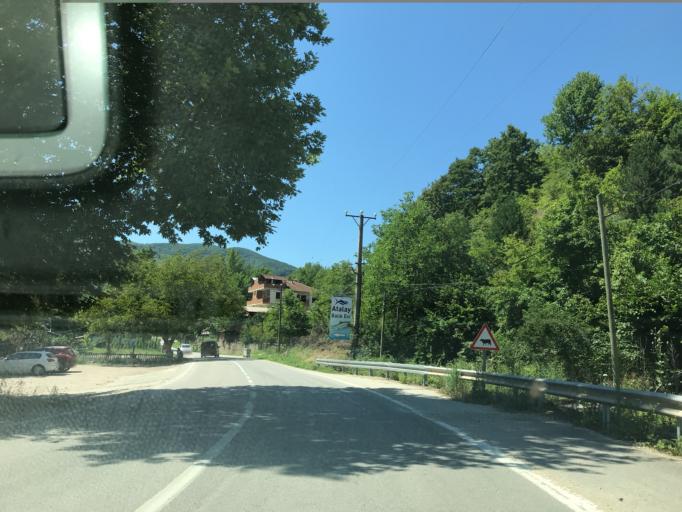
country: TR
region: Bursa
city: Tahtakopru
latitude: 39.9601
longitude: 29.6031
